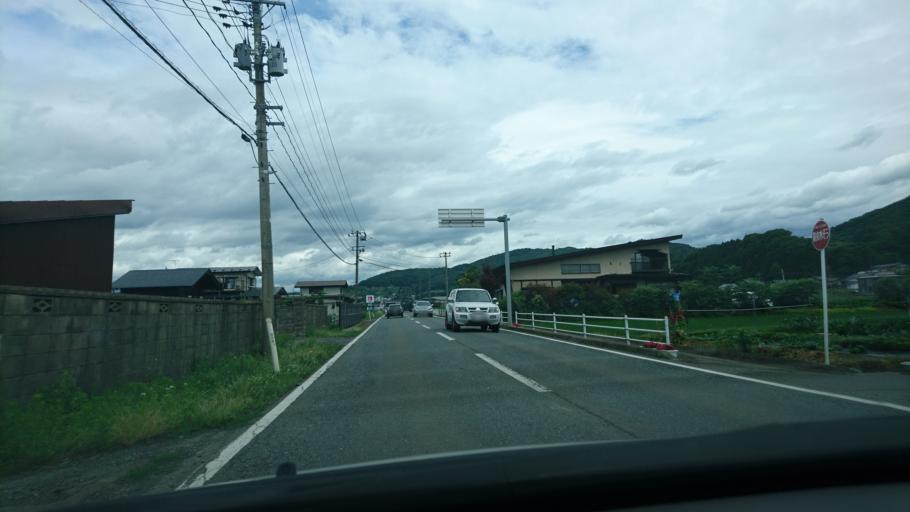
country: JP
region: Iwate
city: Morioka-shi
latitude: 39.6446
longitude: 141.1847
